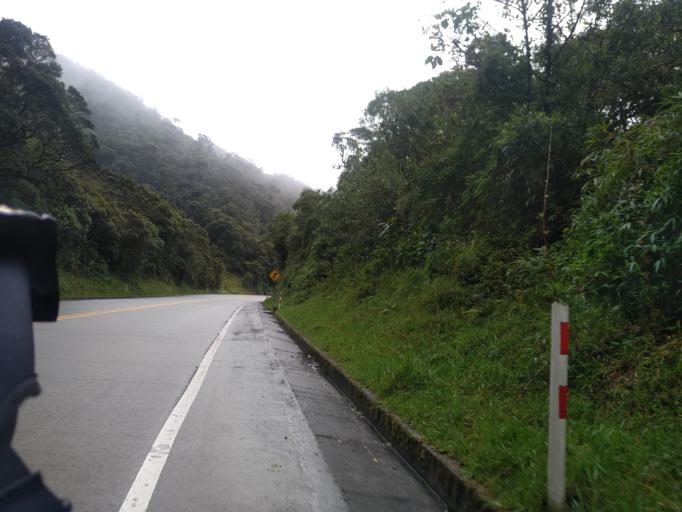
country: EC
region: Loja
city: Loja
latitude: -3.8736
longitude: -79.2680
